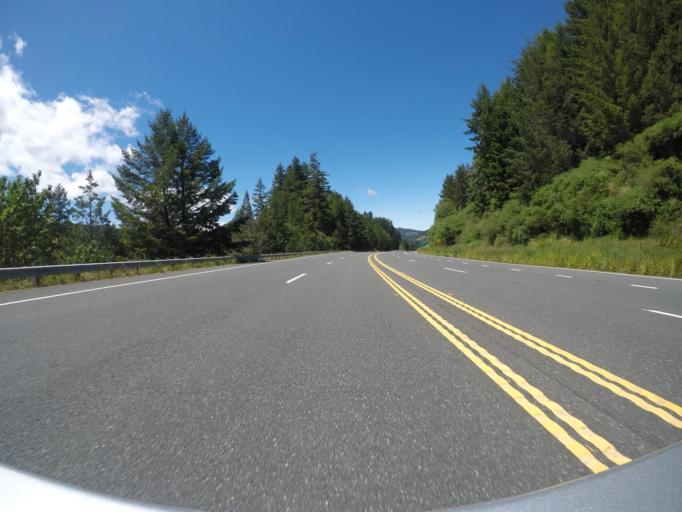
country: US
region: California
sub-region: Humboldt County
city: Redway
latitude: 39.9401
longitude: -123.7773
